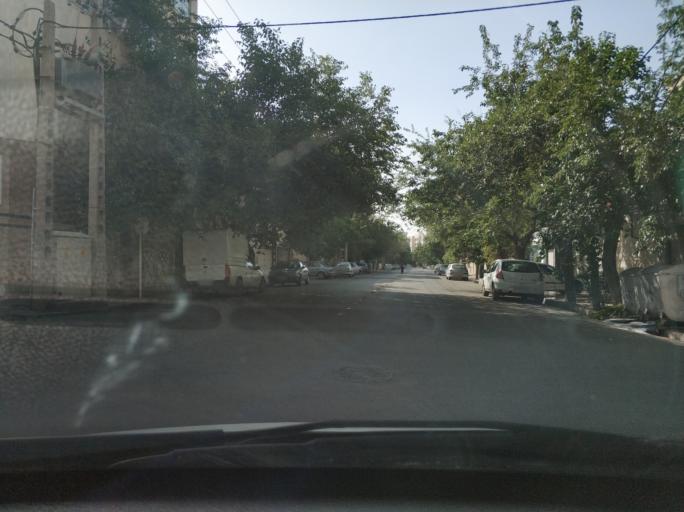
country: IR
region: Razavi Khorasan
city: Mashhad
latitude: 36.2729
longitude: 59.5980
